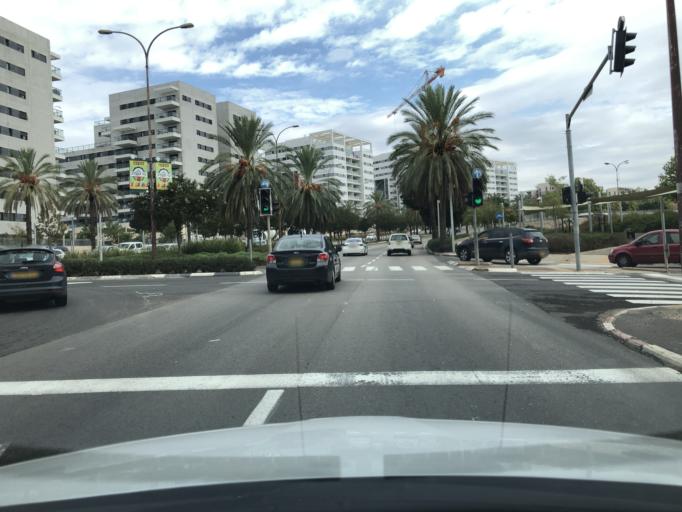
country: IL
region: Central District
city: Modiin
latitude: 31.9086
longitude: 35.0062
